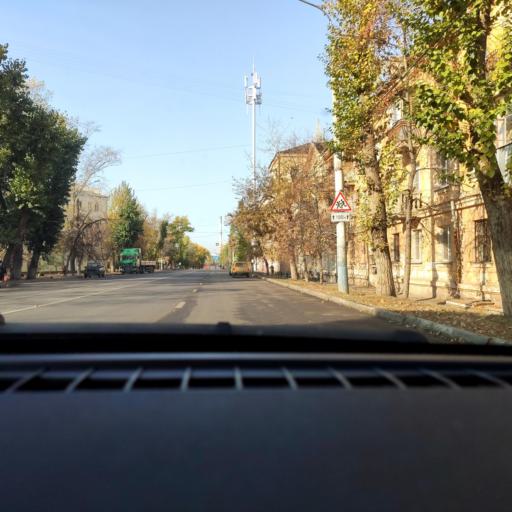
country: RU
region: Voronezj
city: Maslovka
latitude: 51.6207
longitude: 39.2456
